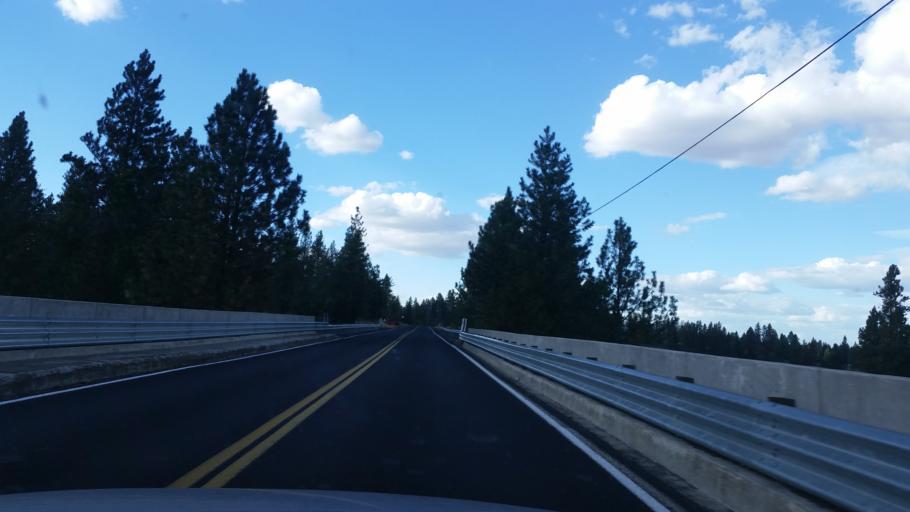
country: US
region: Washington
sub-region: Spokane County
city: Cheney
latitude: 47.4616
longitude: -117.5803
